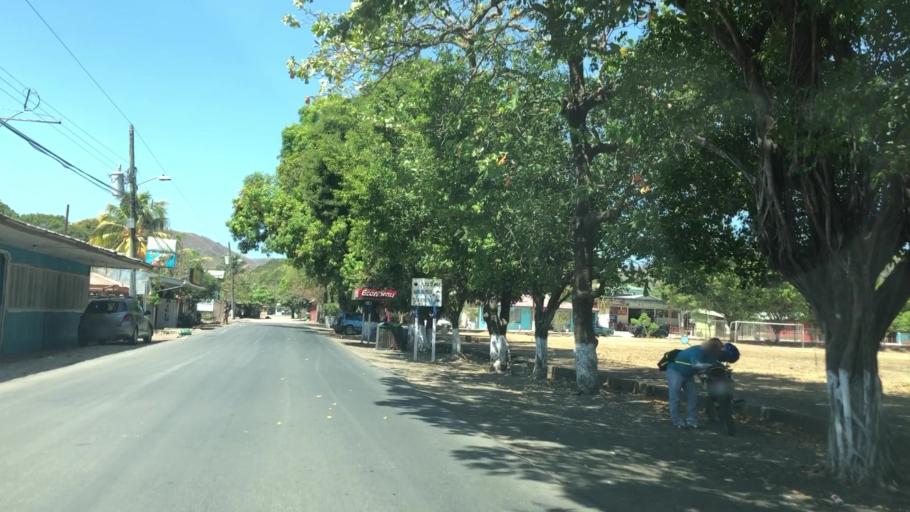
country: CR
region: Guanacaste
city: Sardinal
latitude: 10.3620
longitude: -85.8101
